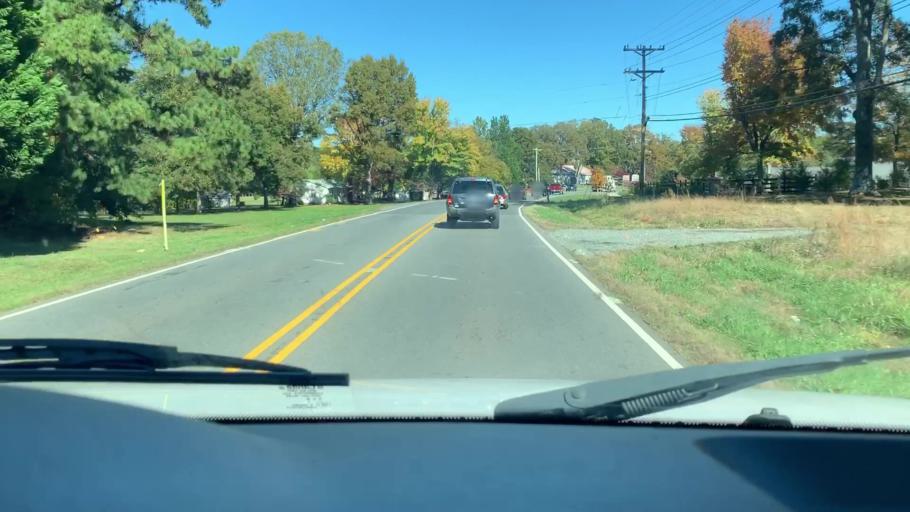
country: US
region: North Carolina
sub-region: Mecklenburg County
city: Huntersville
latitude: 35.4298
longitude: -80.9115
